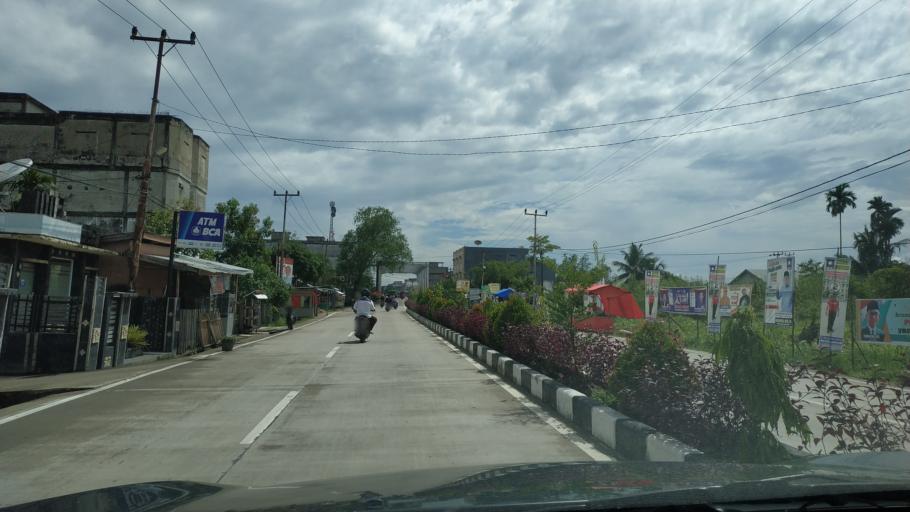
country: ID
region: Riau
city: Tembilahan
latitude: -0.3270
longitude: 103.1434
